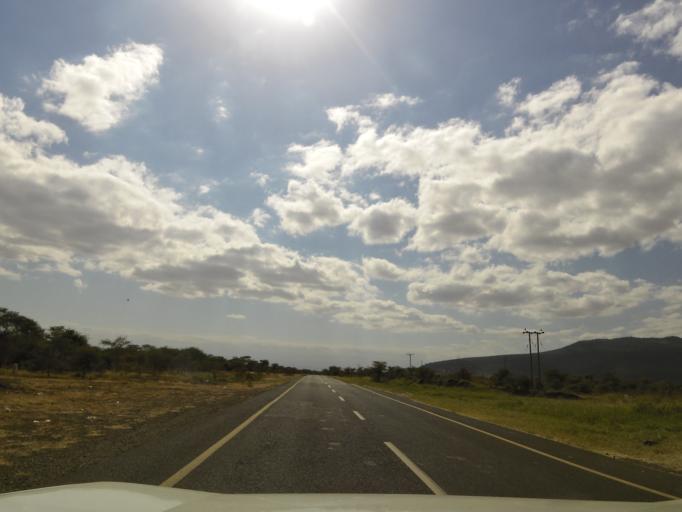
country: TZ
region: Arusha
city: Mto wa Mbu
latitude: -3.5052
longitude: 36.0112
